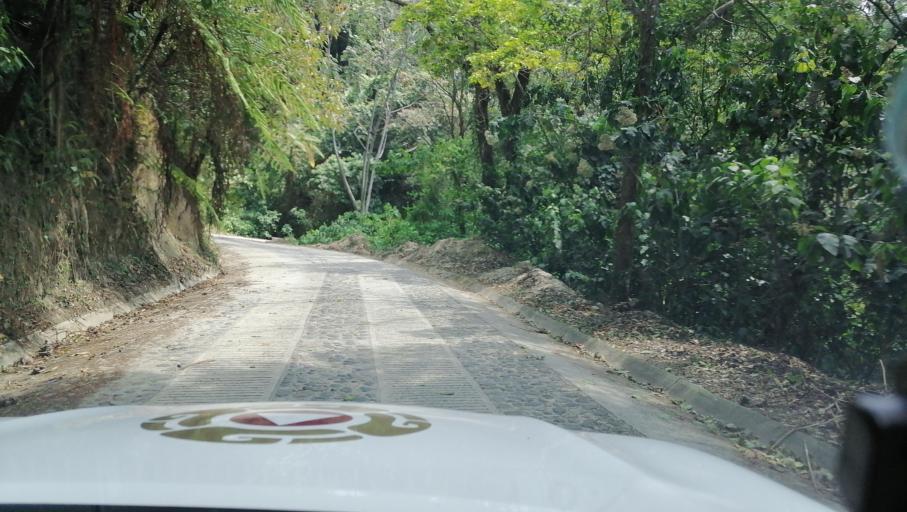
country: MX
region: Chiapas
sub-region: Tapachula
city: Canton Villaflor
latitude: 15.1342
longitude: -92.2920
